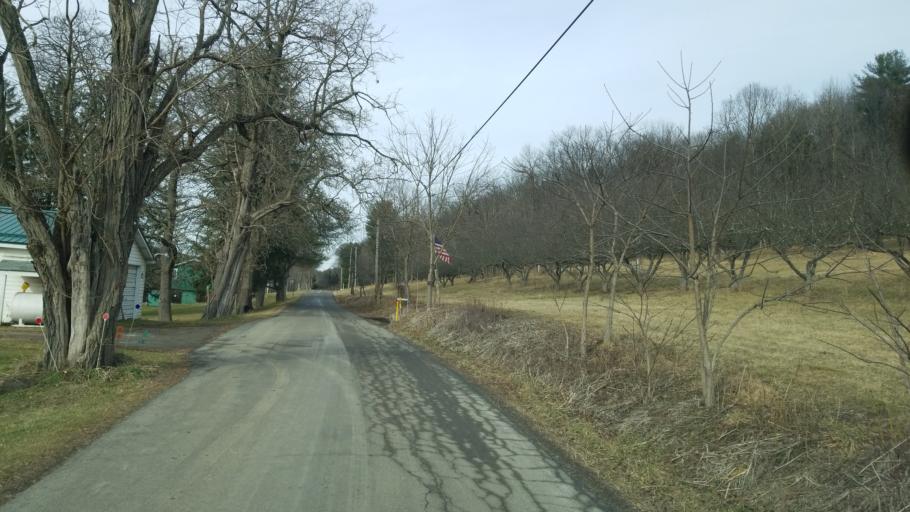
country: US
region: Pennsylvania
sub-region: Jefferson County
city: Punxsutawney
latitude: 40.8310
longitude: -78.9870
